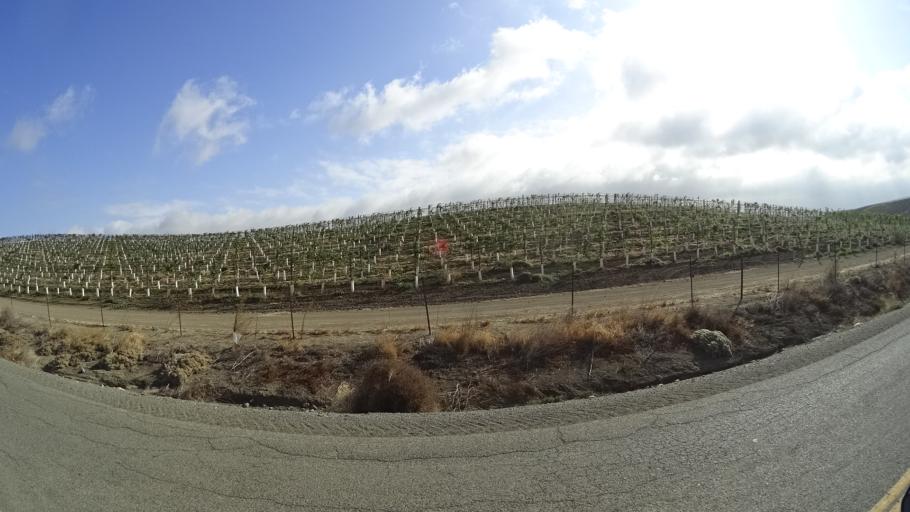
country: US
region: California
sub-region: Yolo County
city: Dunnigan
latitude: 38.7987
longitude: -122.0075
